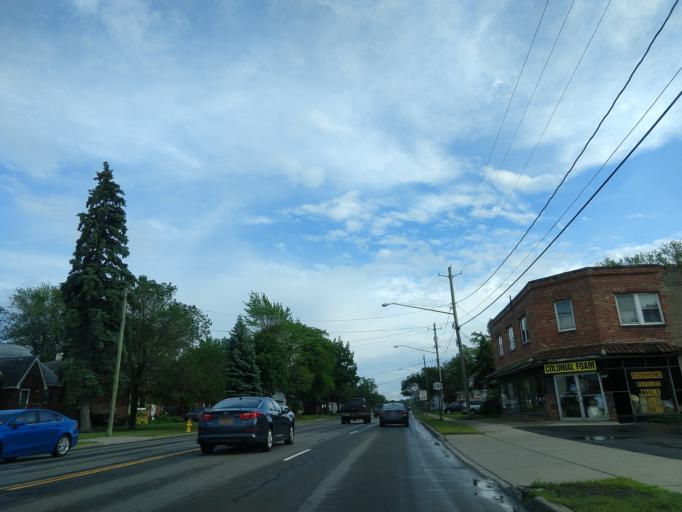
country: US
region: New York
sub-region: Erie County
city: Sloan
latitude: 42.8833
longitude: -78.7847
